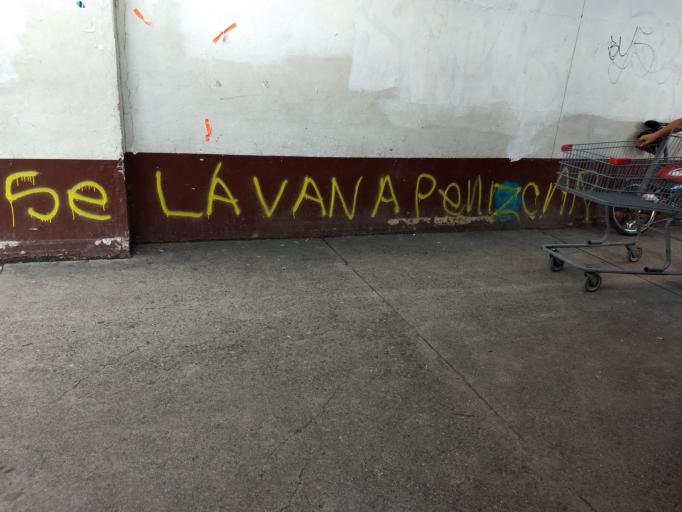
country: MX
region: Jalisco
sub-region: Puerto Vallarta
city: Puerto Vallarta
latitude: 20.6172
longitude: -105.2309
